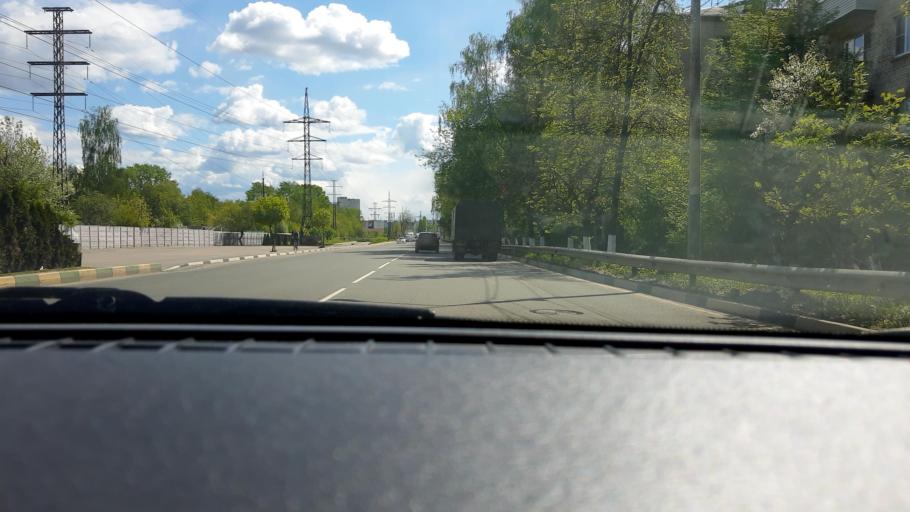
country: RU
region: Nizjnij Novgorod
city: Gorbatovka
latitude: 56.3351
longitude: 43.8565
